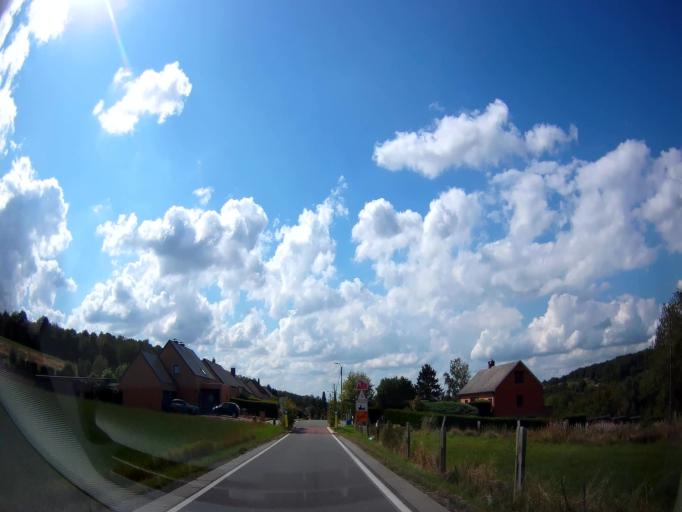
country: BE
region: Wallonia
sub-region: Province de Namur
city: Yvoir
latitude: 50.3530
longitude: 4.9151
